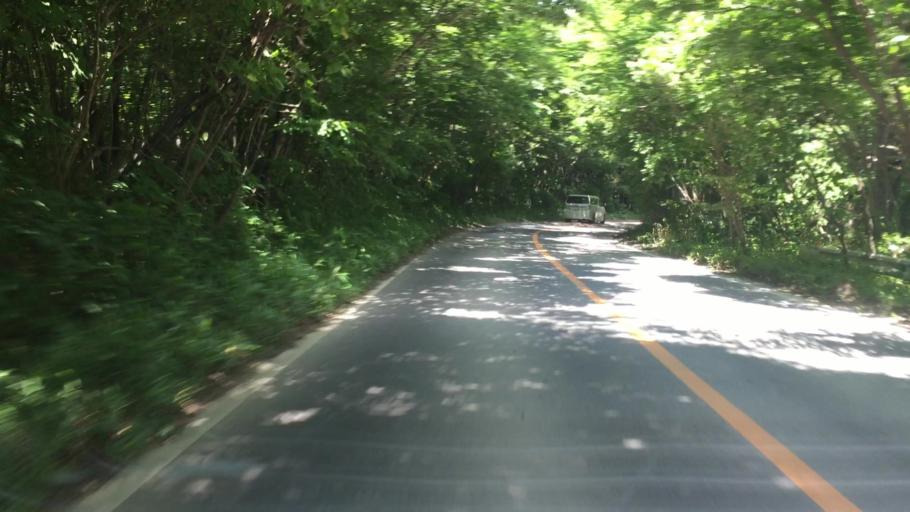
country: JP
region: Tochigi
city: Kuroiso
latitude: 37.0217
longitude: 140.0077
